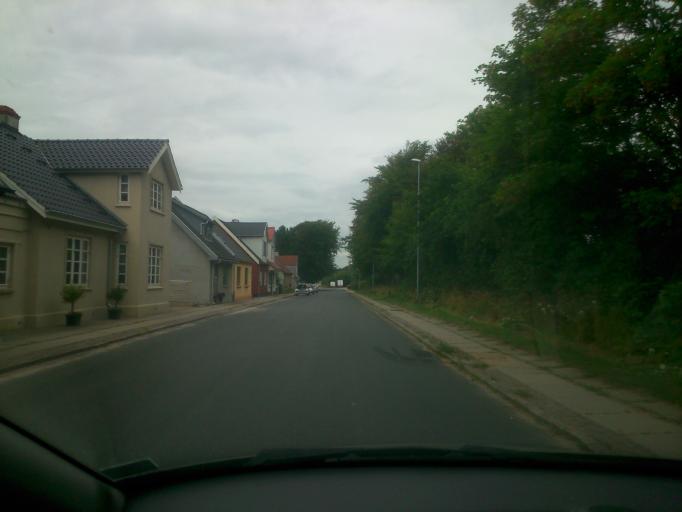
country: DK
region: South Denmark
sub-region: Esbjerg Kommune
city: Esbjerg
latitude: 55.5342
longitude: 8.4410
